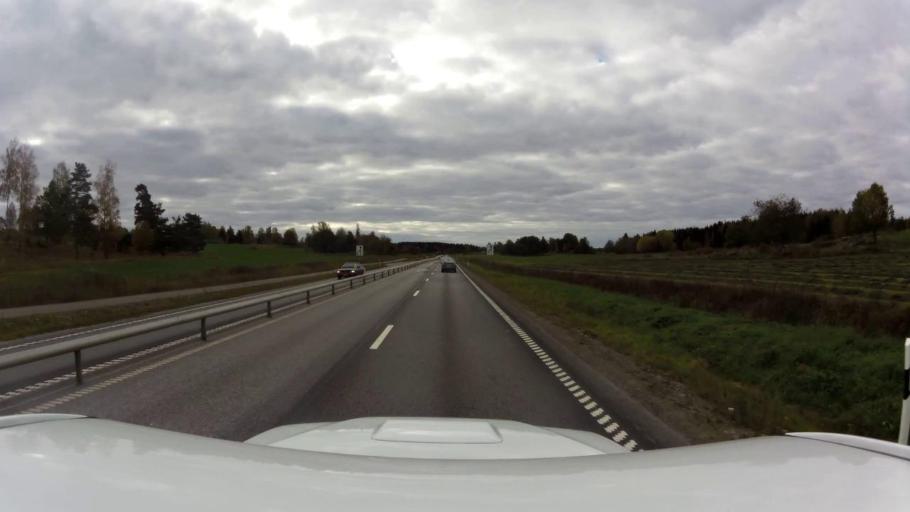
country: SE
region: OEstergoetland
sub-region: Linkopings Kommun
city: Malmslatt
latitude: 58.3169
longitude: 15.5675
